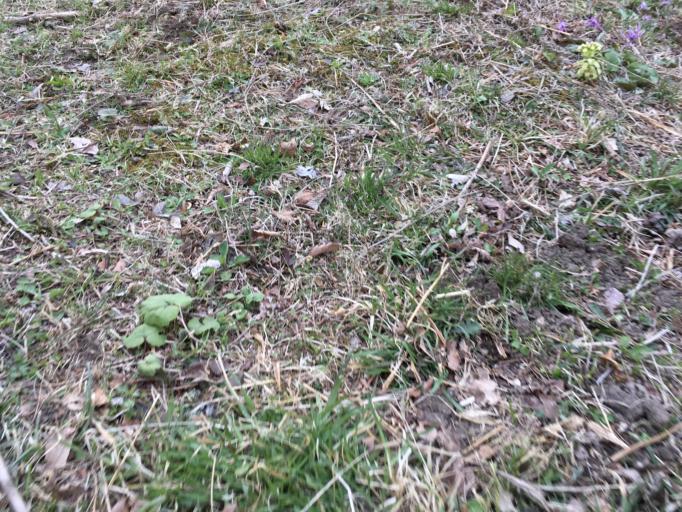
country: JP
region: Iwate
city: Ichinoseki
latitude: 38.9393
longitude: 141.2305
